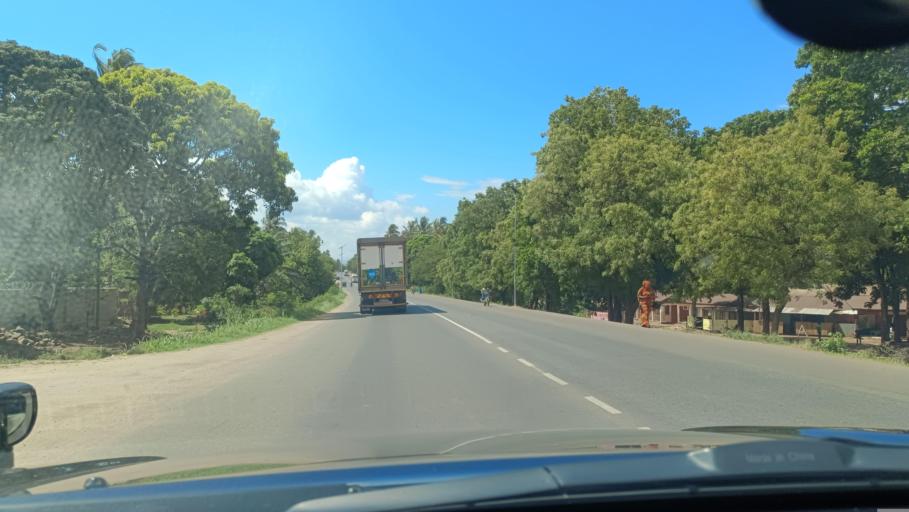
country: TZ
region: Morogoro
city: Morogoro
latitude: -6.8129
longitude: 37.6503
